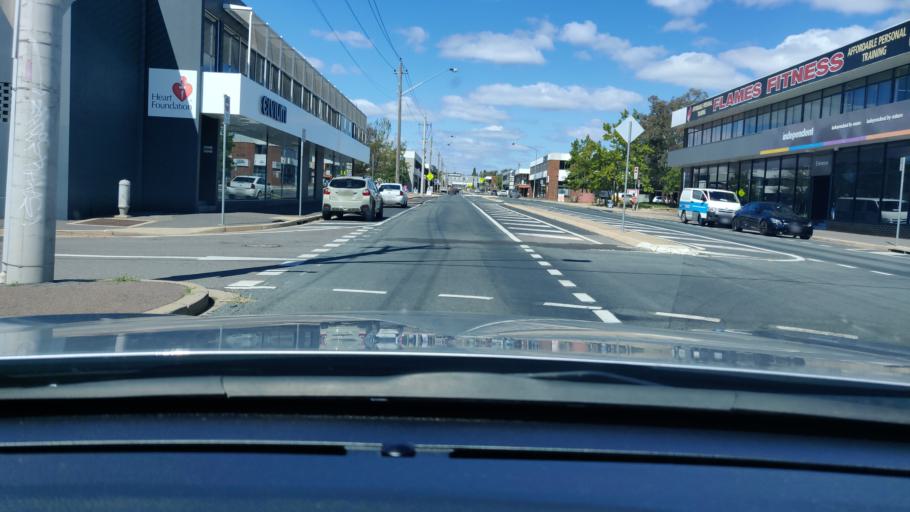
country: AU
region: Australian Capital Territory
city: Forrest
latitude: -35.3515
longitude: 149.0878
